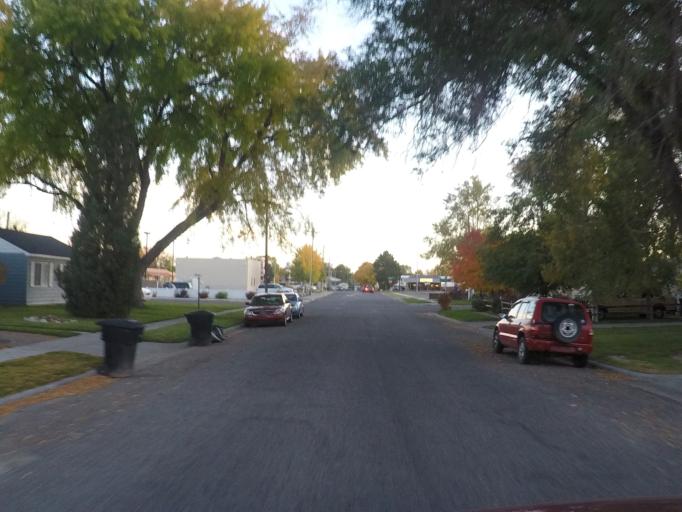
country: US
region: Montana
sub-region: Yellowstone County
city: Billings
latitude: 45.7854
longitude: -108.5436
